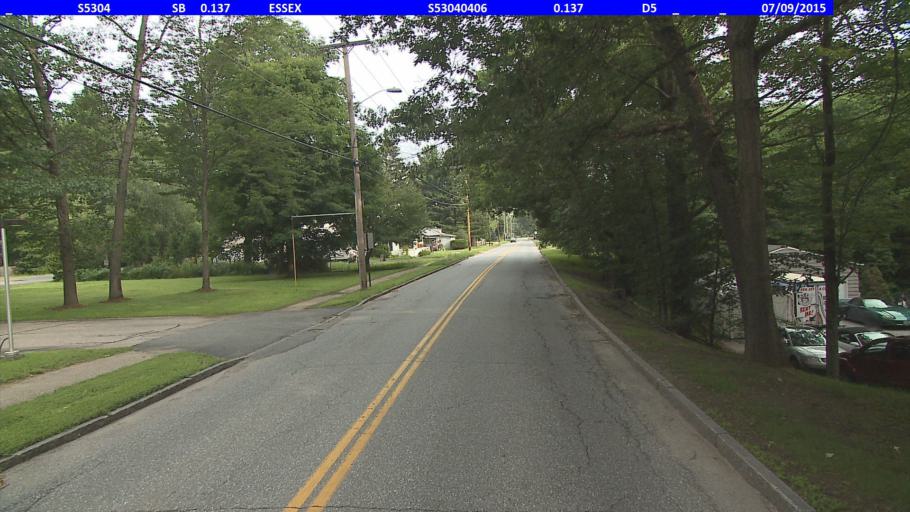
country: US
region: Vermont
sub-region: Chittenden County
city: Essex Junction
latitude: 44.4971
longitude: -73.1309
